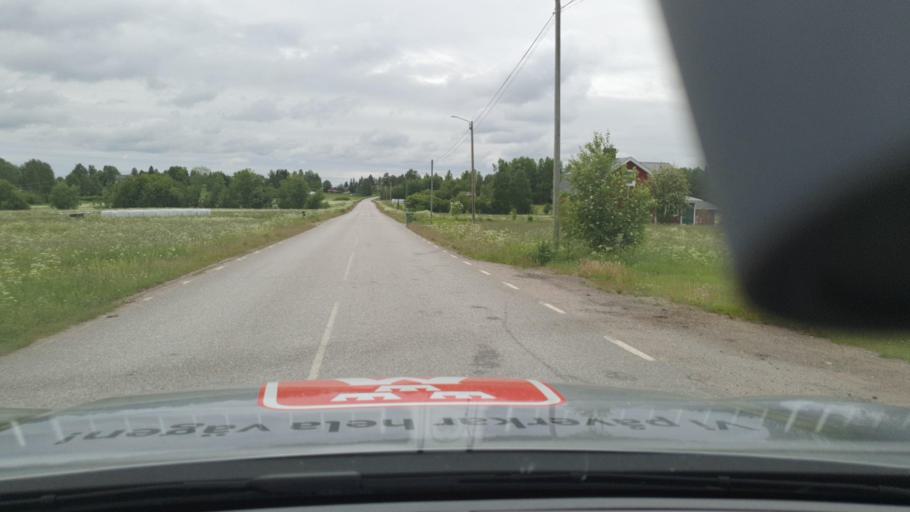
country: SE
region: Norrbotten
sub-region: Lulea Kommun
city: Ranea
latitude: 65.9079
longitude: 22.1761
